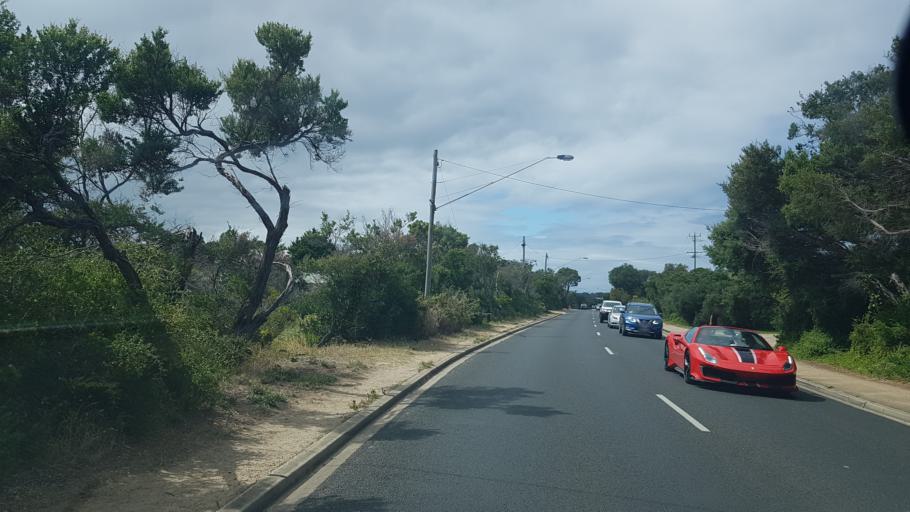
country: AU
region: Victoria
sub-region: Mornington Peninsula
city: Sorrento
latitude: -38.3419
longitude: 144.7375
